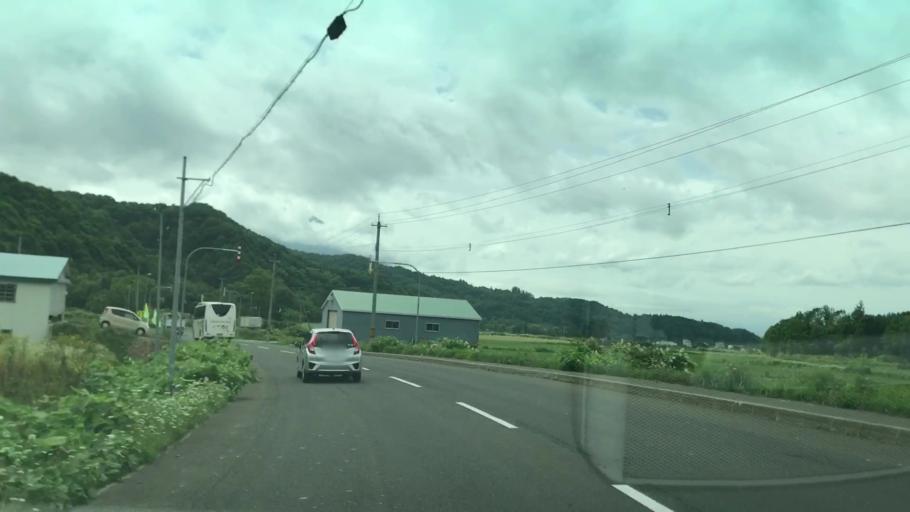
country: JP
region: Hokkaido
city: Niseko Town
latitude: 42.9477
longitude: 140.8225
